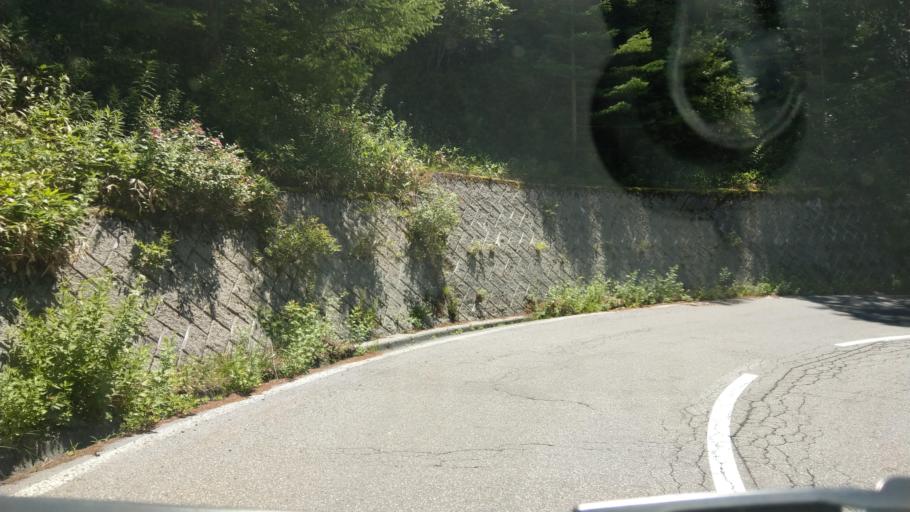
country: JP
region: Nagano
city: Komoro
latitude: 36.3946
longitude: 138.4727
